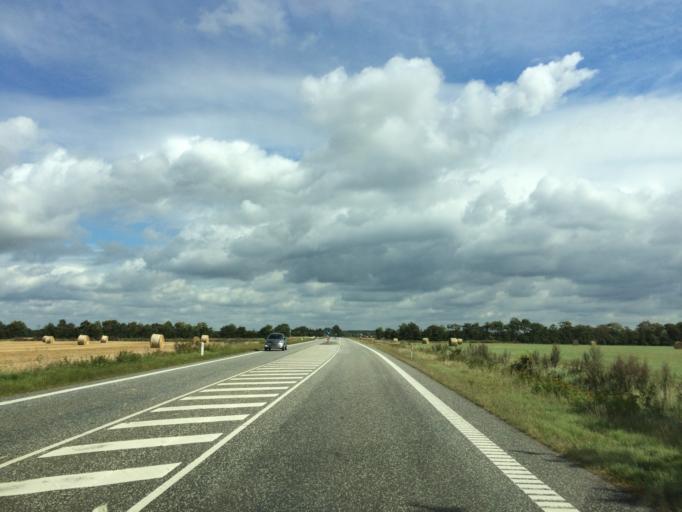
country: DK
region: Central Jutland
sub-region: Holstebro Kommune
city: Vinderup
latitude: 56.3863
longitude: 8.7876
